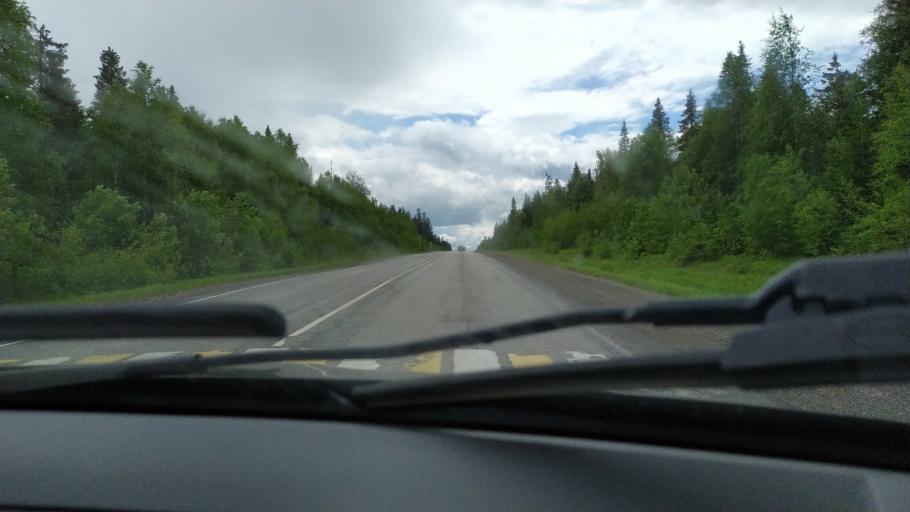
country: RU
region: Perm
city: Gremyachinsk
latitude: 58.5104
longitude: 57.8117
